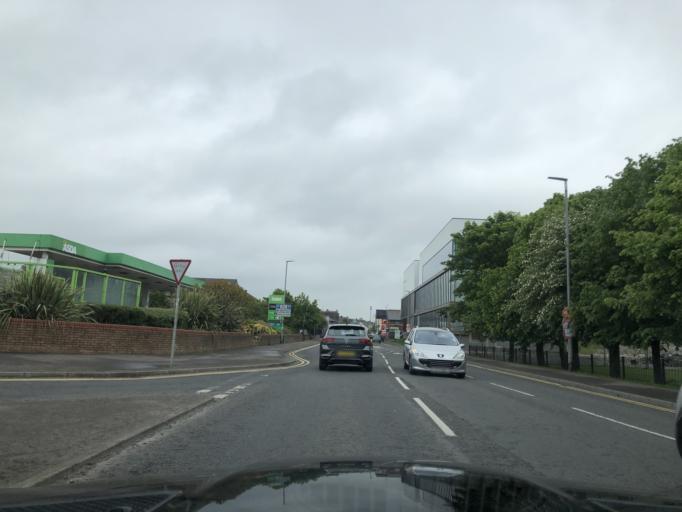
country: GB
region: Northern Ireland
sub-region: Down District
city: Downpatrick
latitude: 54.3235
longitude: -5.7207
